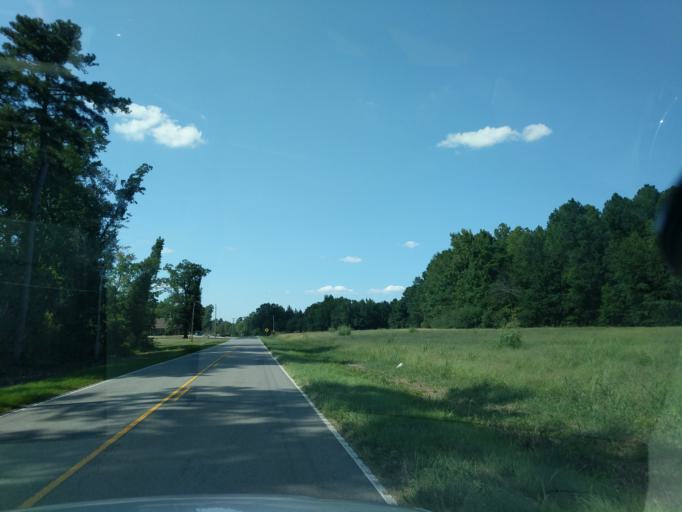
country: US
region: South Carolina
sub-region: Lexington County
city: Leesville
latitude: 34.0167
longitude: -81.5200
